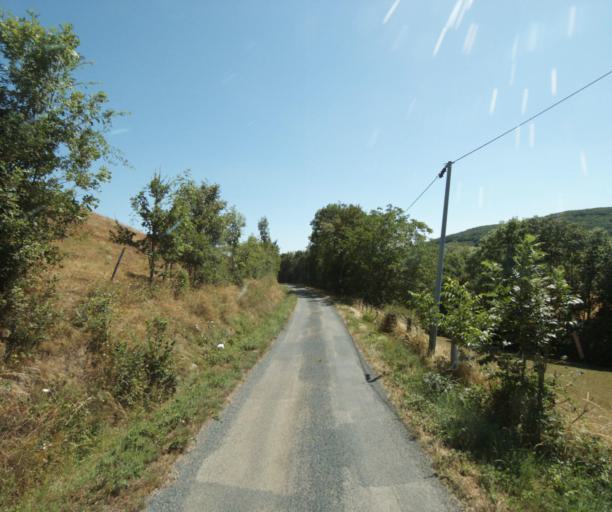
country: FR
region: Rhone-Alpes
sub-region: Departement du Rhone
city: Montrottier
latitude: 45.7898
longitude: 4.5016
